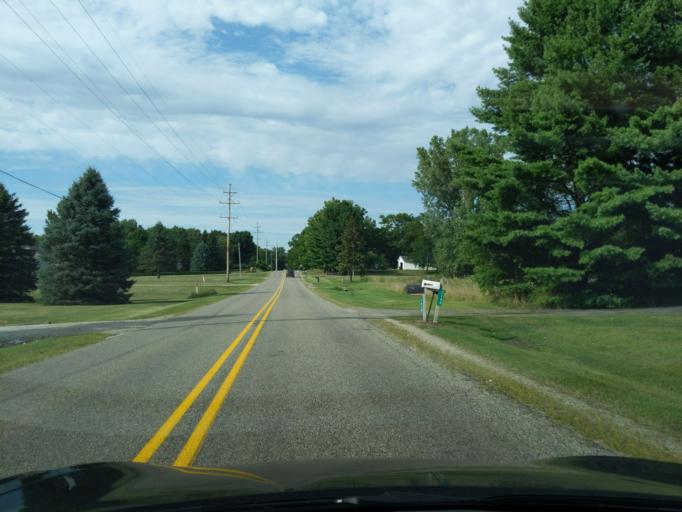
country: US
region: Michigan
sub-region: Eaton County
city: Dimondale
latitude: 42.6720
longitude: -84.6227
